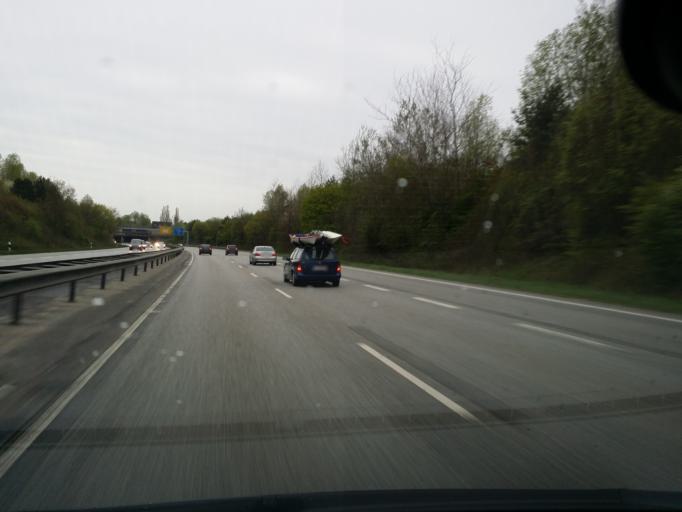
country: DE
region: Schleswig-Holstein
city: Kronshagen
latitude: 54.3235
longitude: 10.0976
